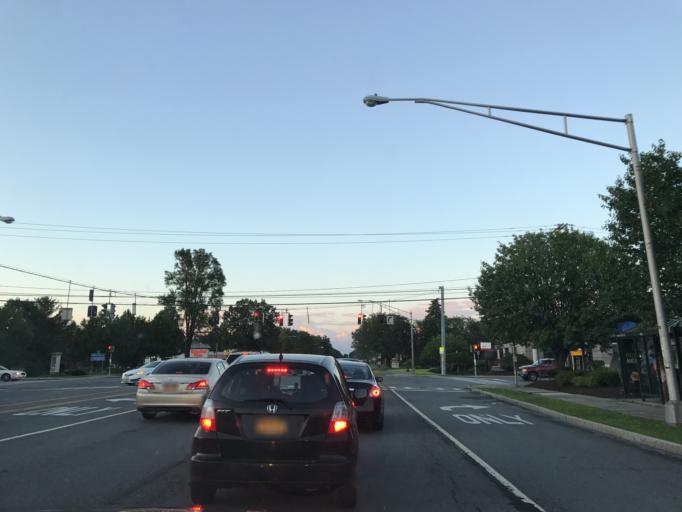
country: US
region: New York
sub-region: Albany County
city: Roessleville
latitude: 42.7153
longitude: -73.8118
